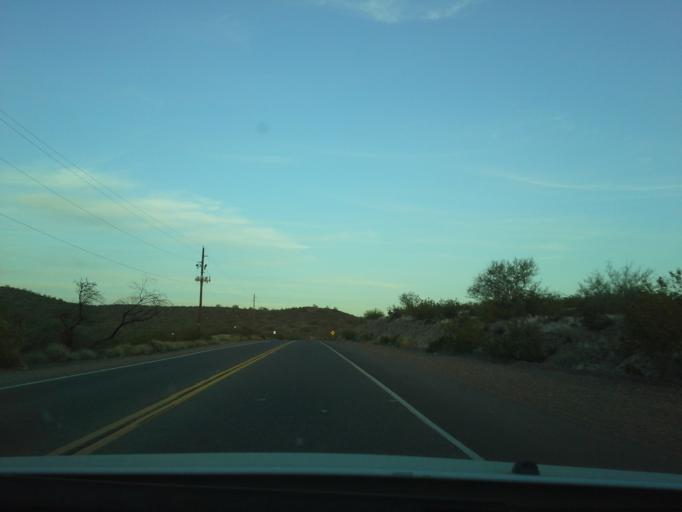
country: US
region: Arizona
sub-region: Maricopa County
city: Anthem
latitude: 33.7129
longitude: -112.0730
